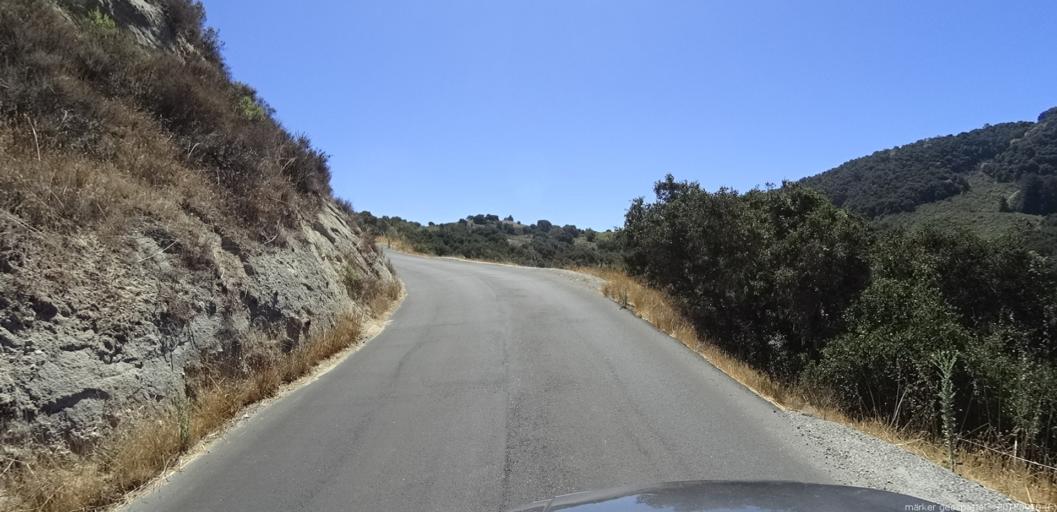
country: US
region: California
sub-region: Monterey County
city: Carmel Valley Village
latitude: 36.4783
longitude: -121.8027
